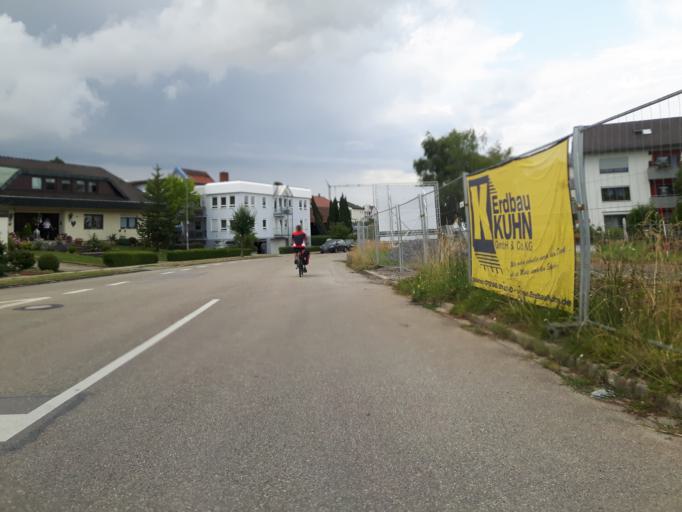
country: DE
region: Baden-Wuerttemberg
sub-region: Regierungsbezirk Stuttgart
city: Eppingen
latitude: 49.1314
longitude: 8.9223
